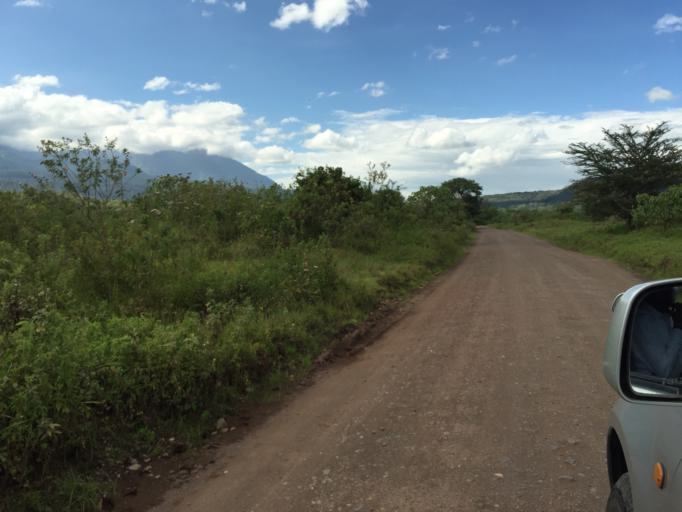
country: TZ
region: Arusha
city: Usa River
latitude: -3.3103
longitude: 36.8796
